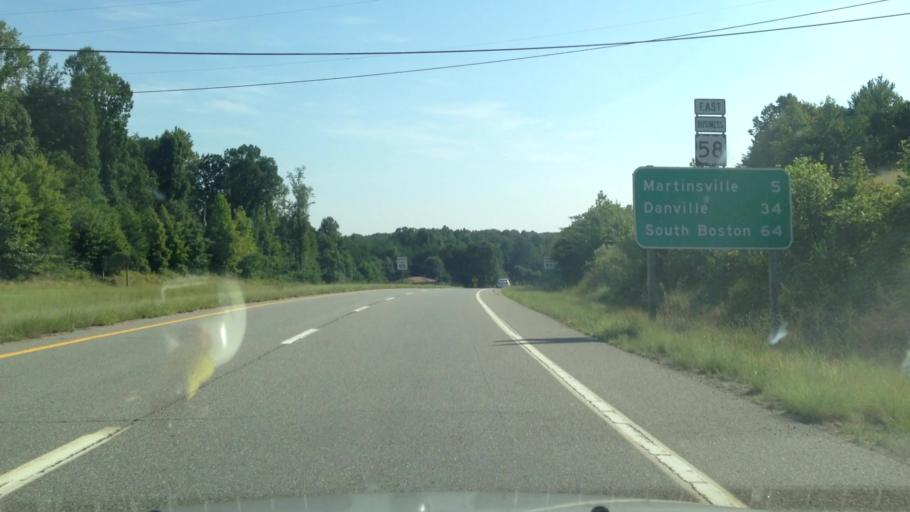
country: US
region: Virginia
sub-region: Henry County
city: Horse Pasture
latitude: 36.6500
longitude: -79.9133
